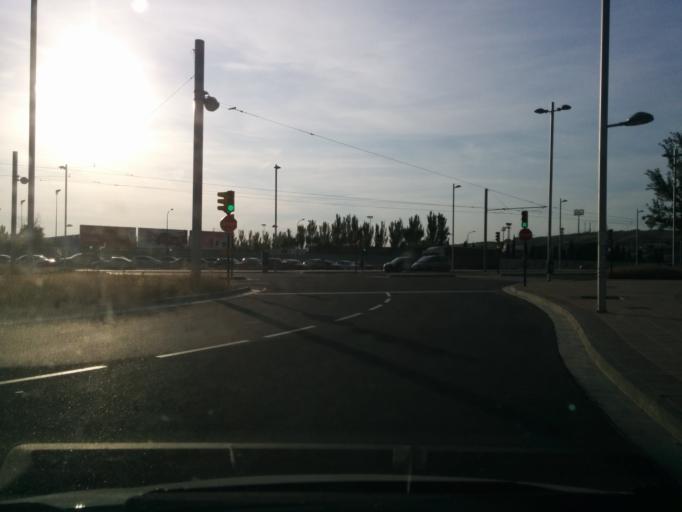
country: ES
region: Aragon
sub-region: Provincia de Zaragoza
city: Almozara
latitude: 41.6812
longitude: -0.8895
